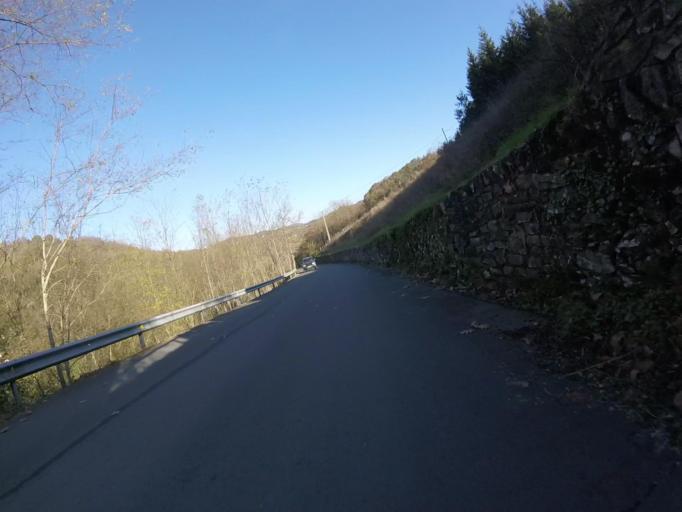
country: ES
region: Navarre
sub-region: Provincia de Navarra
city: Igantzi
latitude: 43.2366
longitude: -1.7032
